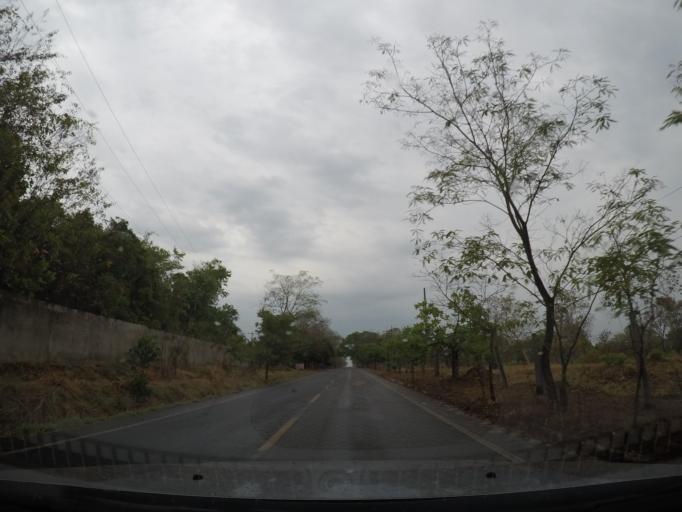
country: BR
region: Goias
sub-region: Pirenopolis
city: Pirenopolis
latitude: -15.8495
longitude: -48.9293
